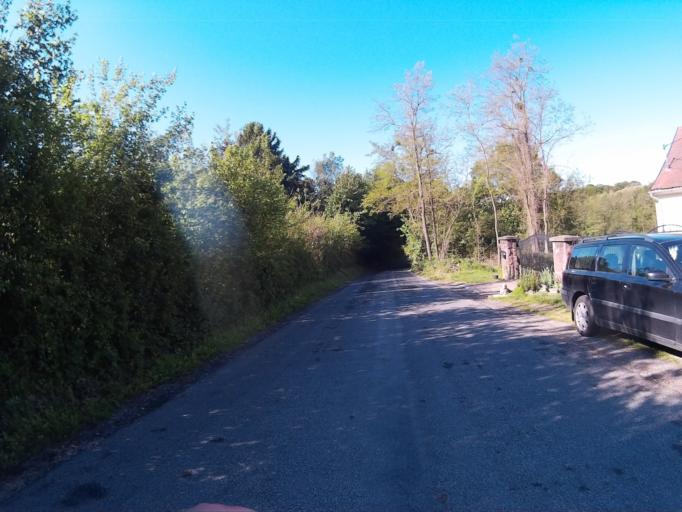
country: HU
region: Vas
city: Kormend
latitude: 46.9880
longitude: 16.6699
